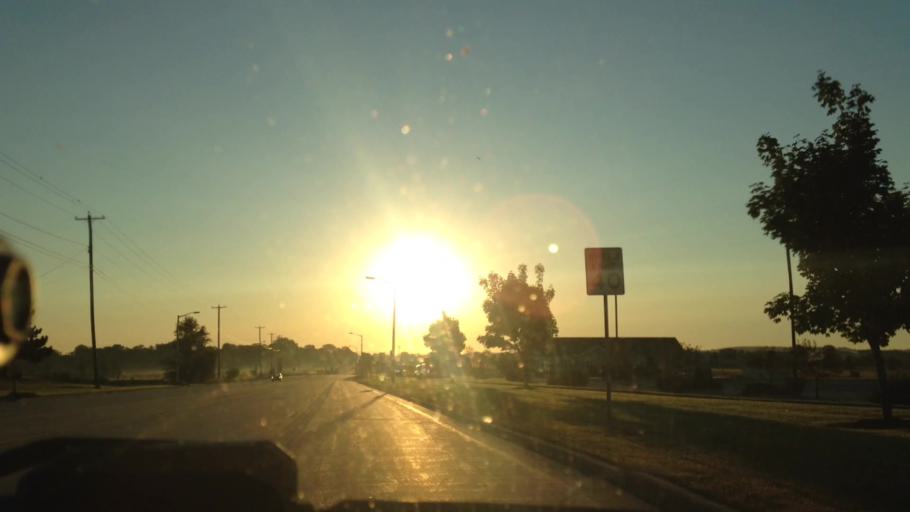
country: US
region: Wisconsin
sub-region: Washington County
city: West Bend
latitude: 43.4266
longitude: -88.1461
